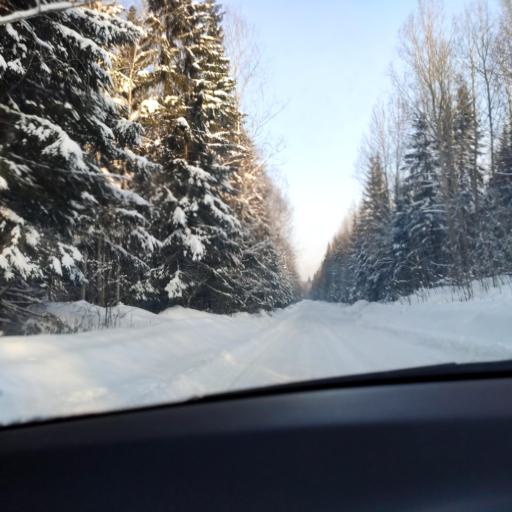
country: RU
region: Perm
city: Kondratovo
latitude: 58.0793
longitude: 56.1305
